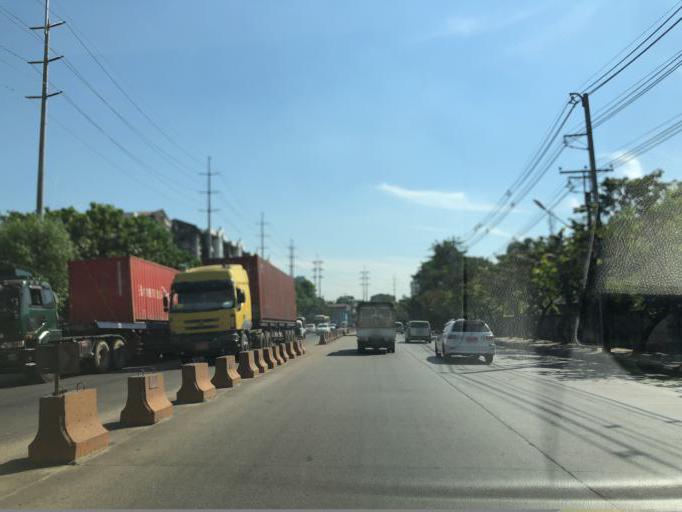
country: MM
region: Yangon
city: Yangon
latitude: 16.8271
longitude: 96.1227
